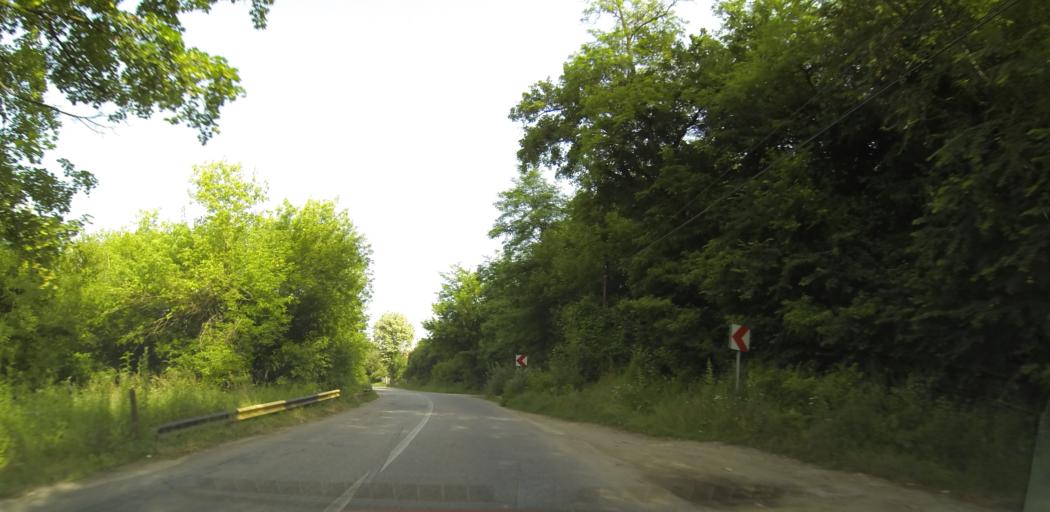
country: RO
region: Valcea
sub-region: Comuna Pausesti-Maglasi
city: Pausesti-Maglasi
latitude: 45.1296
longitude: 24.2650
